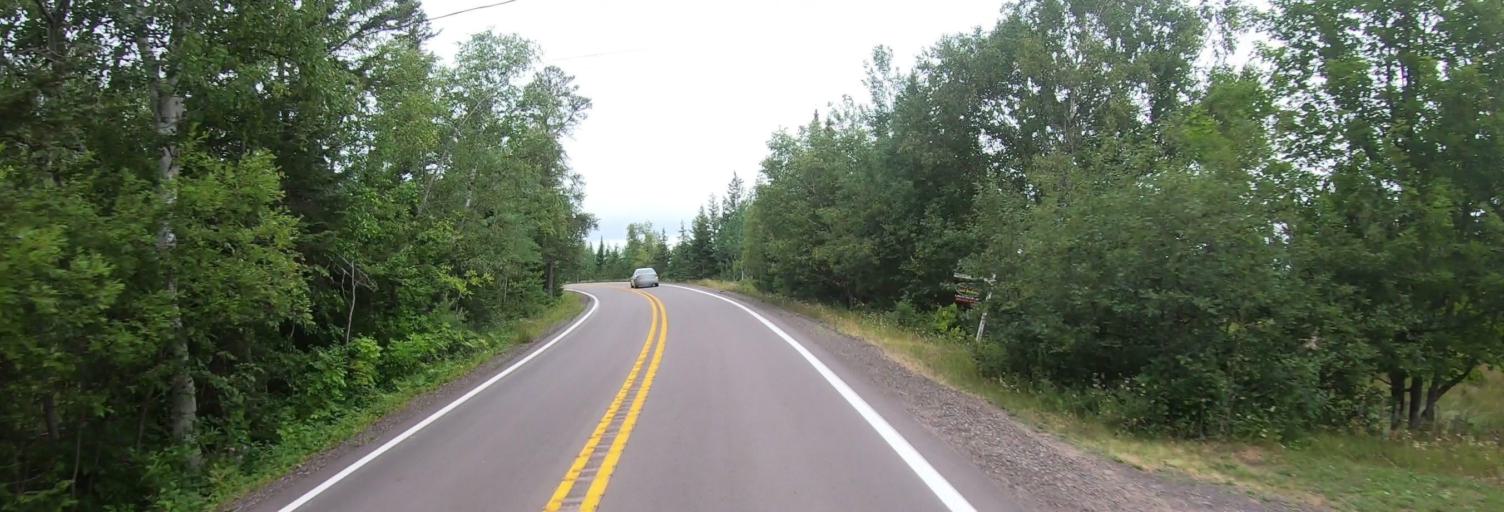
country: US
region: Michigan
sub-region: Keweenaw County
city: Eagle River
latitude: 47.4769
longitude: -88.0107
